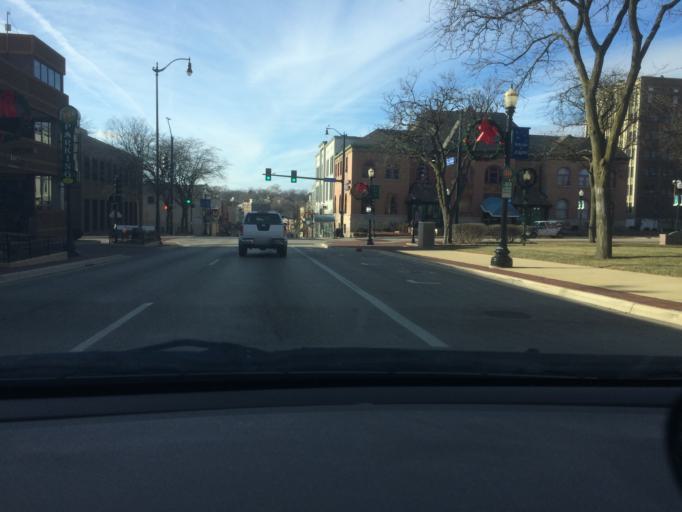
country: US
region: Illinois
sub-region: Kane County
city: Elgin
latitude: 42.0382
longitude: -88.2818
